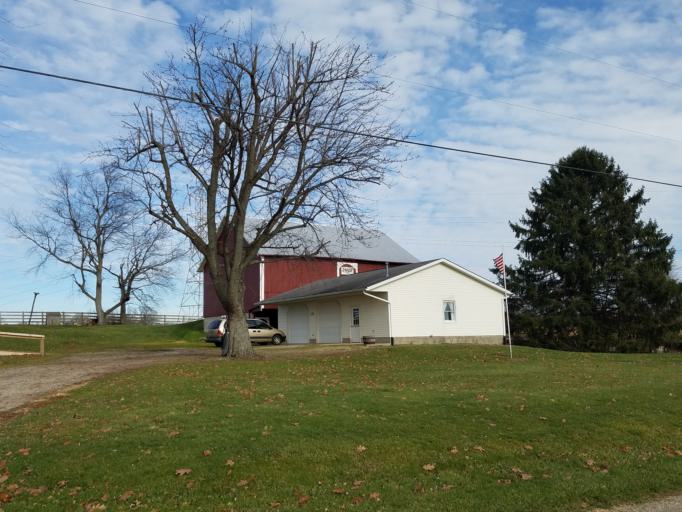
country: US
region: Ohio
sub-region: Knox County
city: Gambier
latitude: 40.4924
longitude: -82.3815
